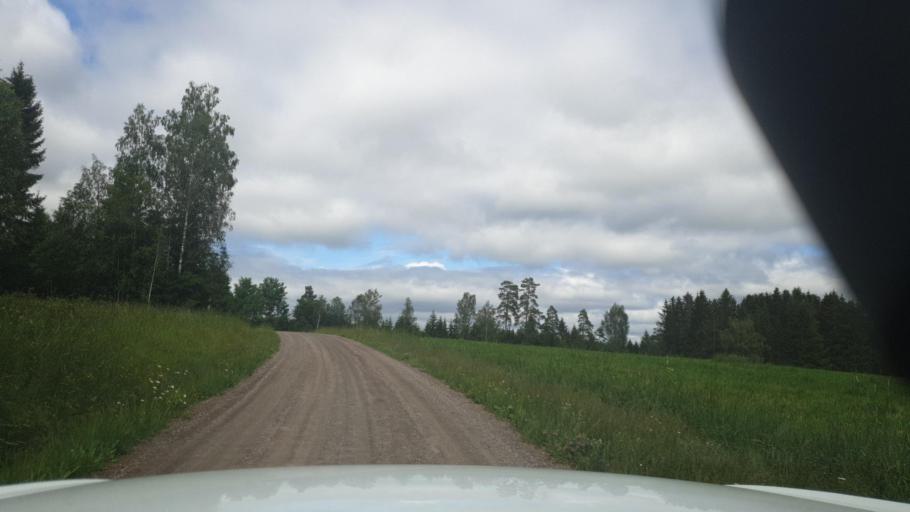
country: SE
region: Vaermland
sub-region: Eda Kommun
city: Charlottenberg
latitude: 59.7349
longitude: 12.1477
